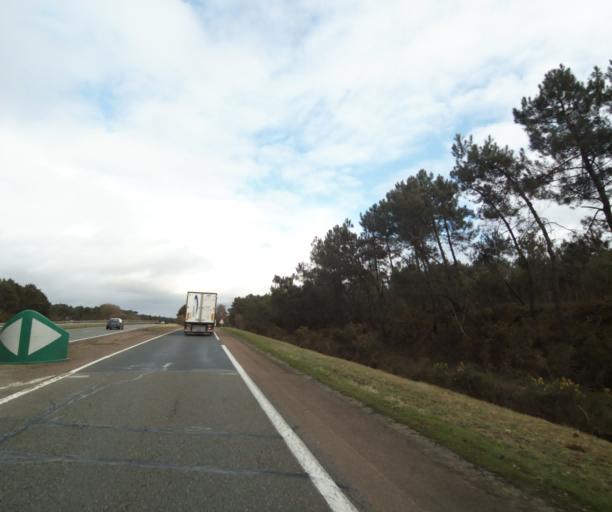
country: FR
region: Pays de la Loire
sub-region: Departement de la Sarthe
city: Ruaudin
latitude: 47.9720
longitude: 0.2400
